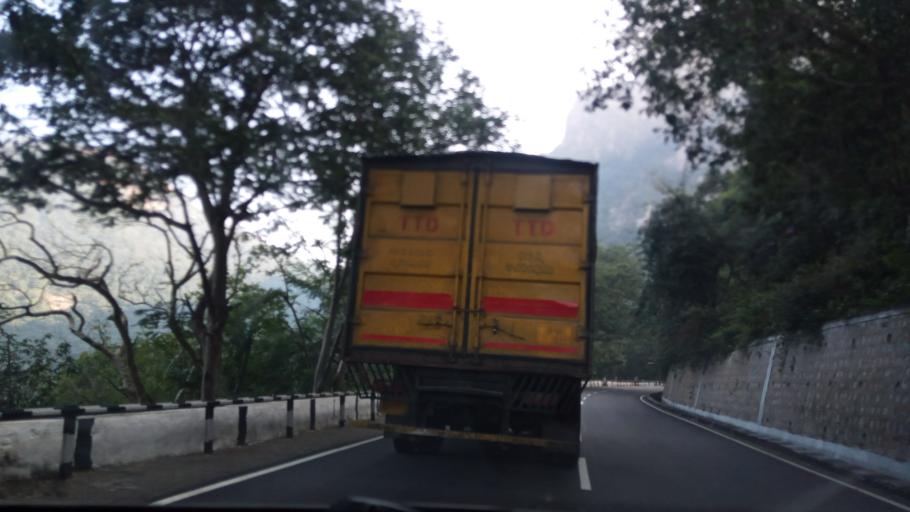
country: IN
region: Andhra Pradesh
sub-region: Chittoor
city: Tirumala
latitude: 13.6587
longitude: 79.3480
